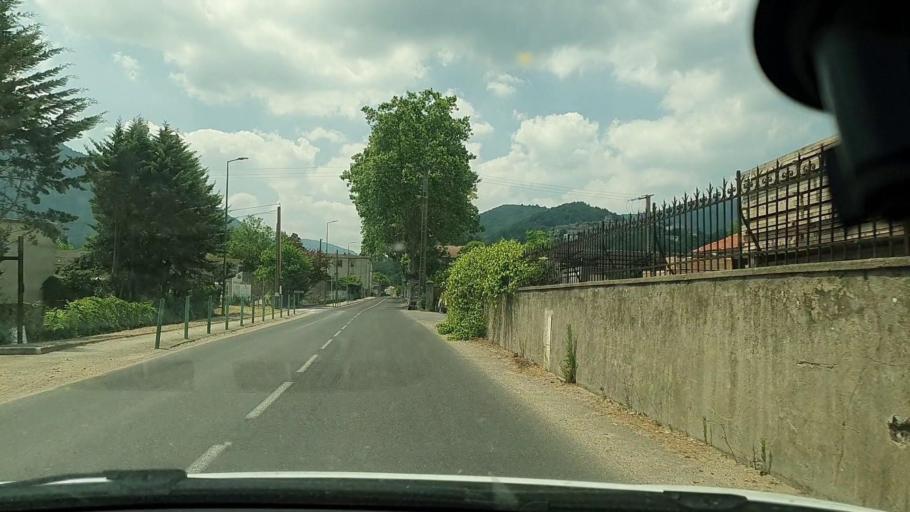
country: FR
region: Languedoc-Roussillon
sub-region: Departement du Gard
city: Aveze
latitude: 43.9736
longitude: 3.5868
